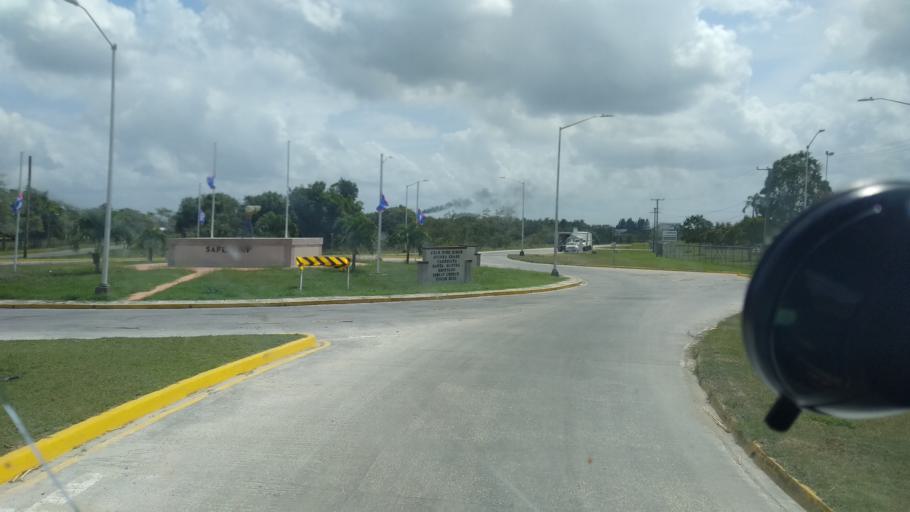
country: BZ
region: Orange Walk
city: Orange Walk
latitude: 18.0555
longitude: -88.5659
